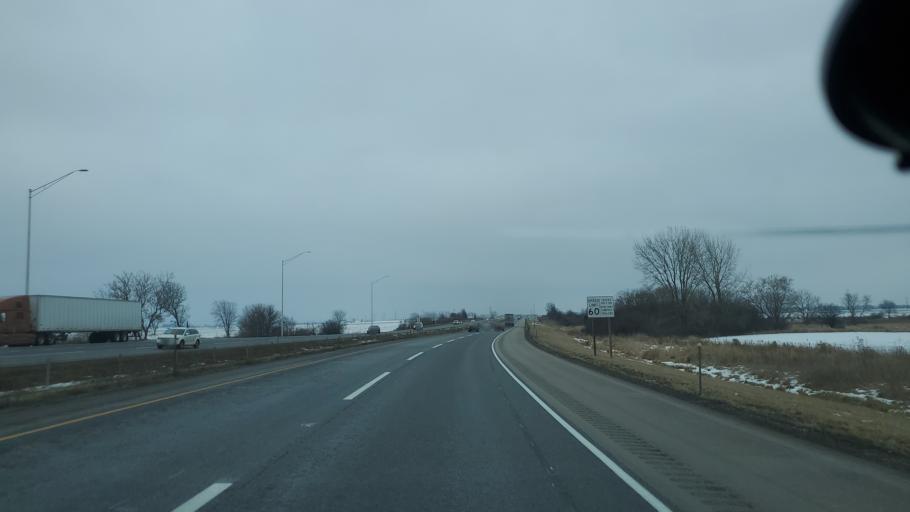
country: US
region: Illinois
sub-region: Kane County
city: Sugar Grove
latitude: 41.8165
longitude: -88.4588
